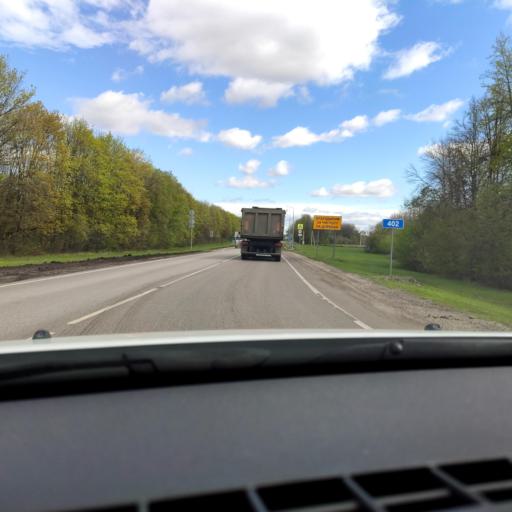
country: RU
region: Lipetsk
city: Yelets
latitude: 52.5395
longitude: 38.7312
